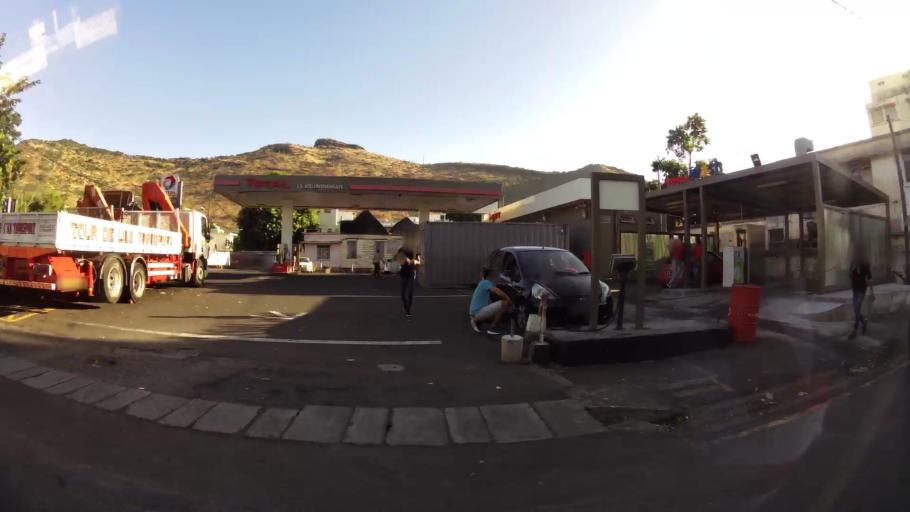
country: MU
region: Port Louis
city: Port Louis
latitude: -20.1695
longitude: 57.5042
